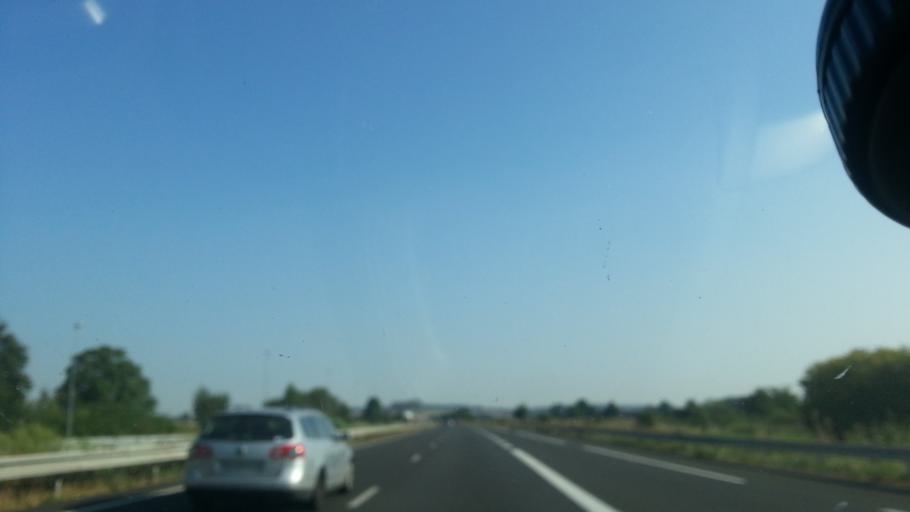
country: FR
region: Poitou-Charentes
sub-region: Departement de la Vienne
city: Antran
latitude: 46.8390
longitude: 0.5251
